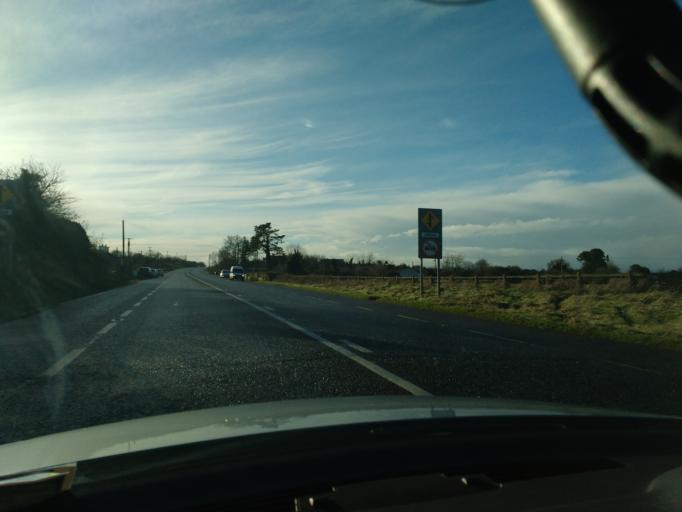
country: IE
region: Munster
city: Thurles
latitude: 52.6516
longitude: -7.7159
